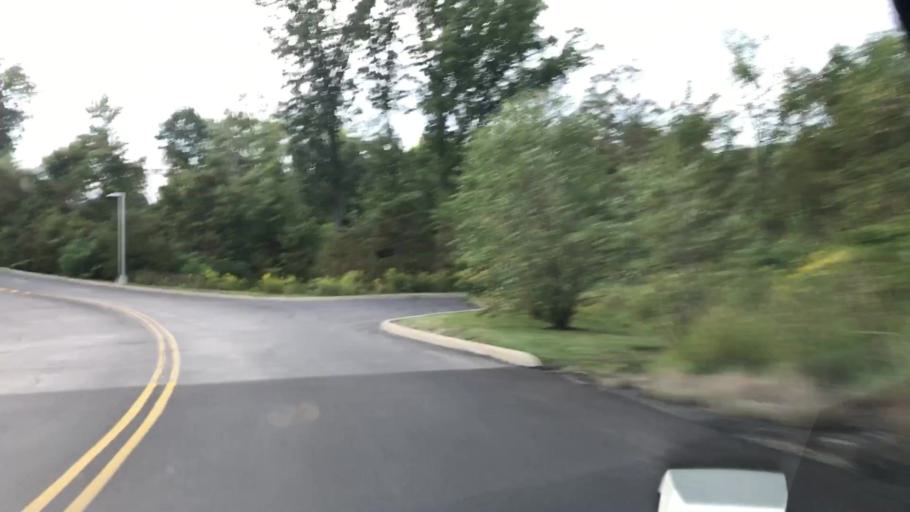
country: US
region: Pennsylvania
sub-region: Allegheny County
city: Carnot-Moon
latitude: 40.5101
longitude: -80.2684
